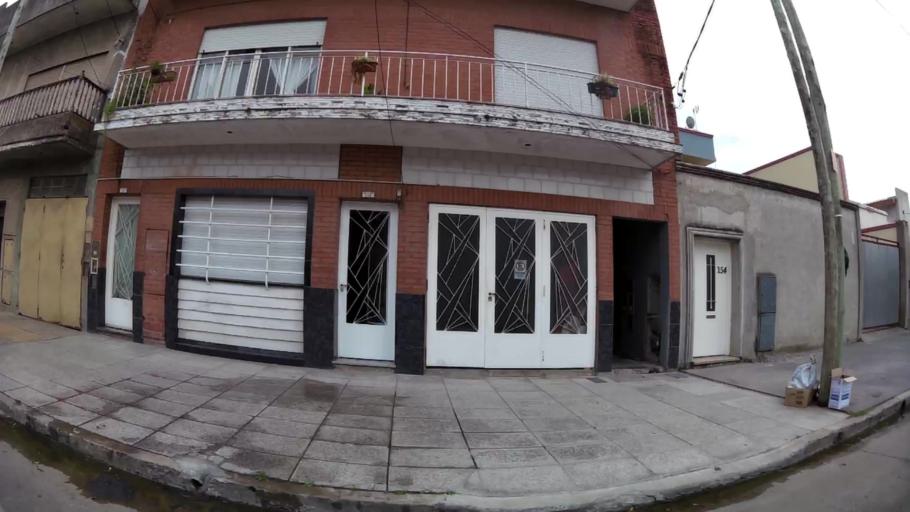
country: AR
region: Buenos Aires F.D.
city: Villa Lugano
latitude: -34.6909
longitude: -58.5136
